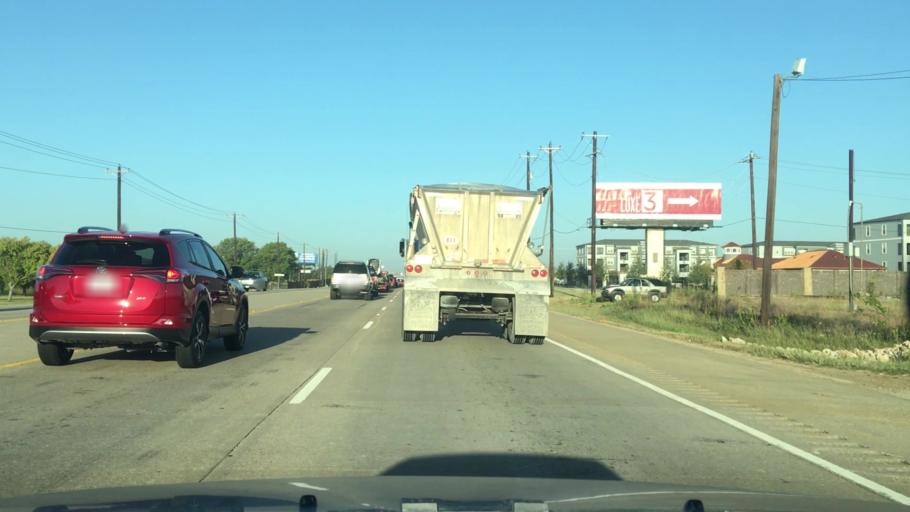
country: US
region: Texas
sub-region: Denton County
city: Cross Roads
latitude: 33.2233
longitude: -96.9720
